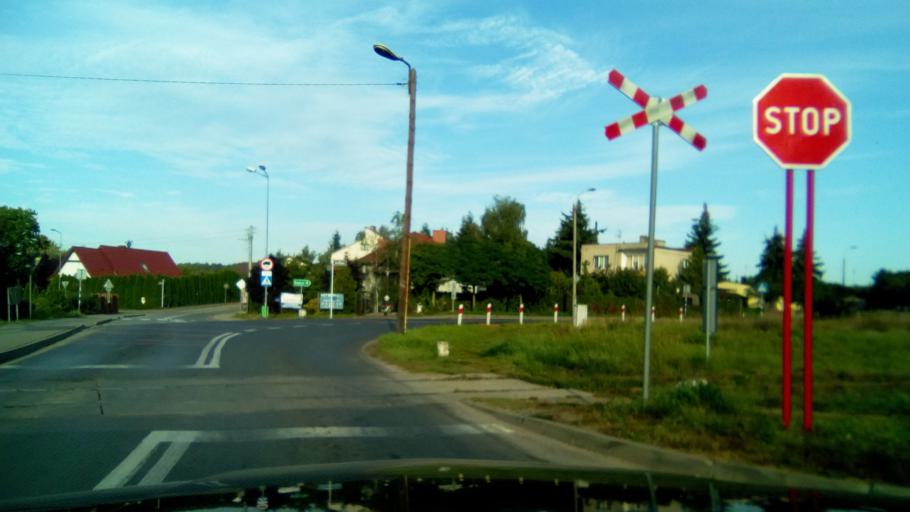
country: PL
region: Greater Poland Voivodeship
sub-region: Powiat wagrowiecki
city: Wagrowiec
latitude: 52.8154
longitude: 17.1860
